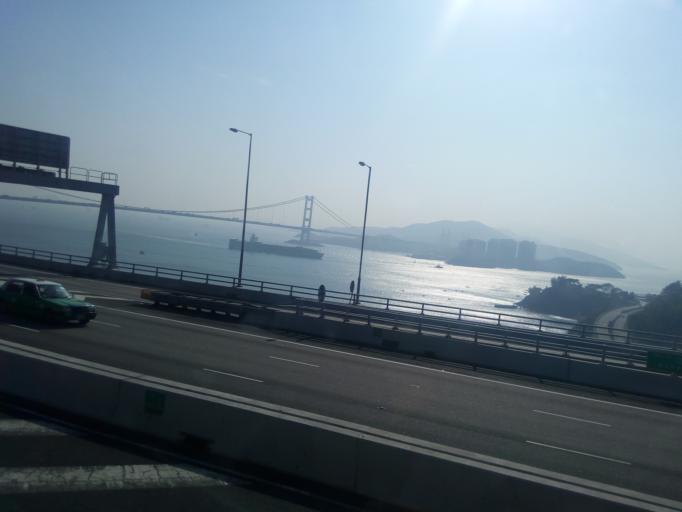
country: HK
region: Tsuen Wan
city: Tsuen Wan
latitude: 22.3692
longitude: 114.0770
